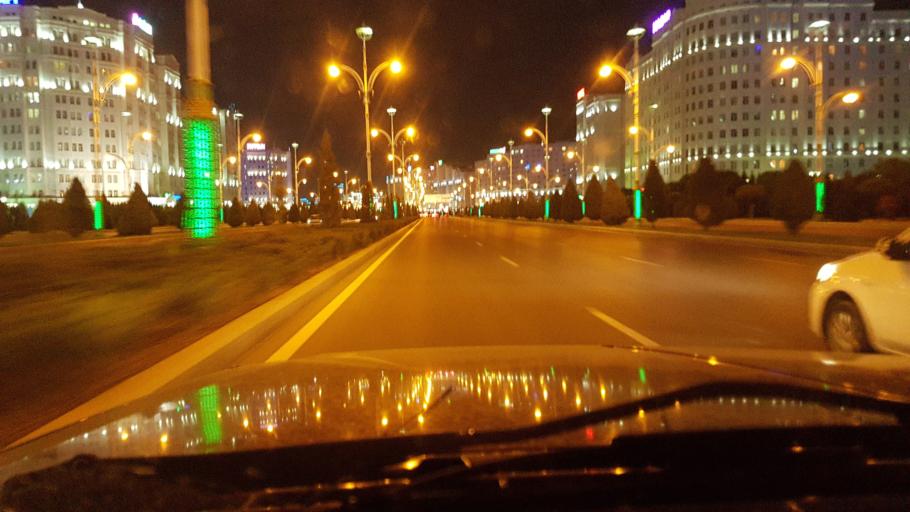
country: TM
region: Ahal
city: Ashgabat
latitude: 37.9019
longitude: 58.3445
